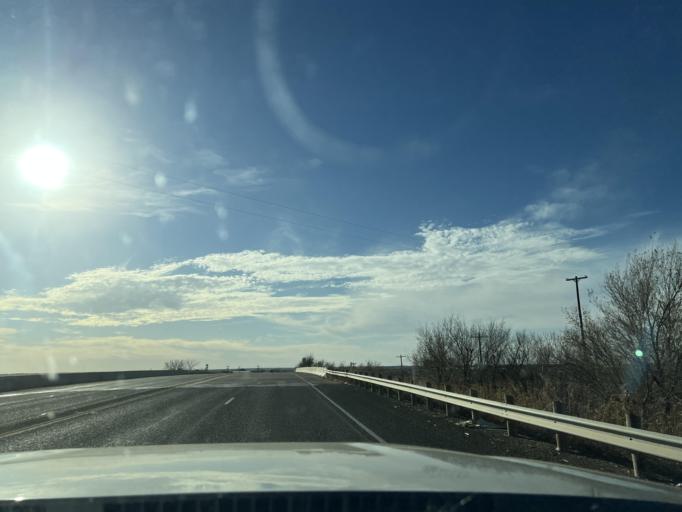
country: US
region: Texas
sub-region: Scurry County
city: Snyder
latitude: 32.7038
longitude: -100.8731
